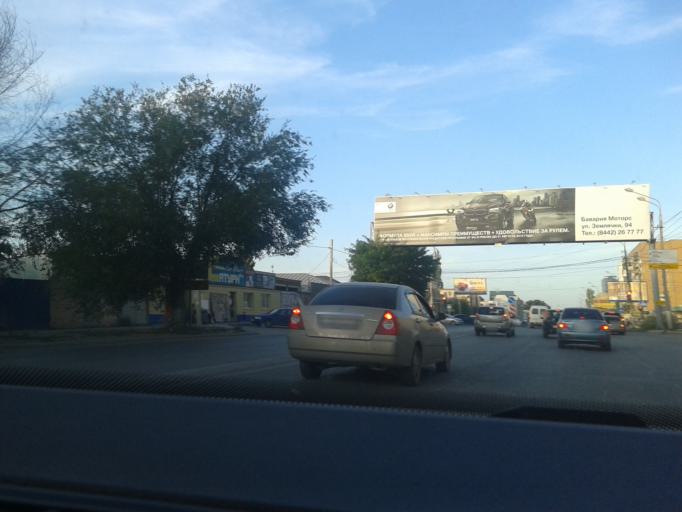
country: RU
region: Volgograd
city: Volgograd
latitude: 48.7217
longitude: 44.5105
